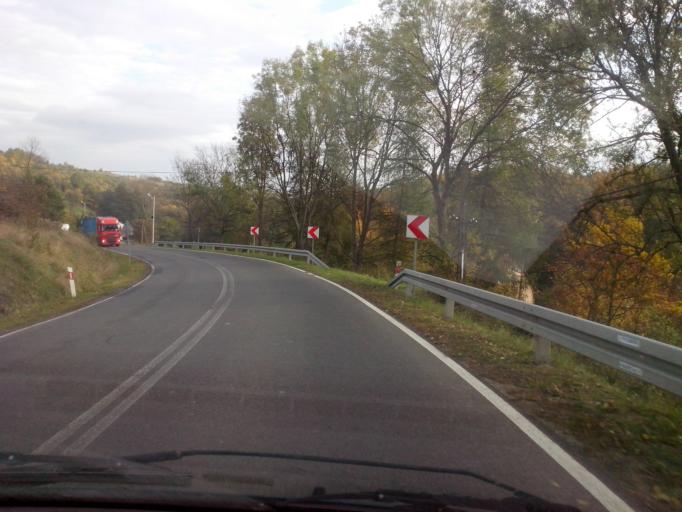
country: PL
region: Subcarpathian Voivodeship
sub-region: Powiat ropczycko-sedziszowski
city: Wielopole Skrzynskie
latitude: 49.9084
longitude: 21.6198
